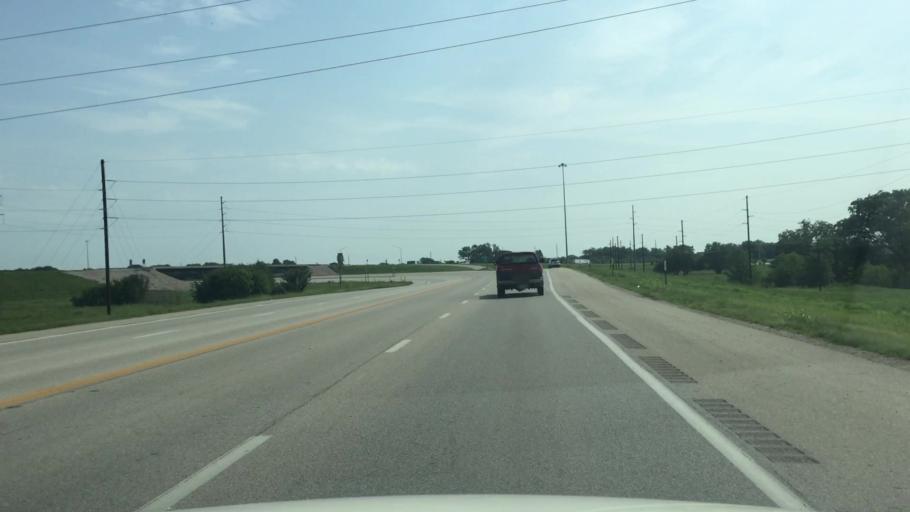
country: US
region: Kansas
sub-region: Montgomery County
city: Coffeyville
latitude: 37.0433
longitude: -95.5869
